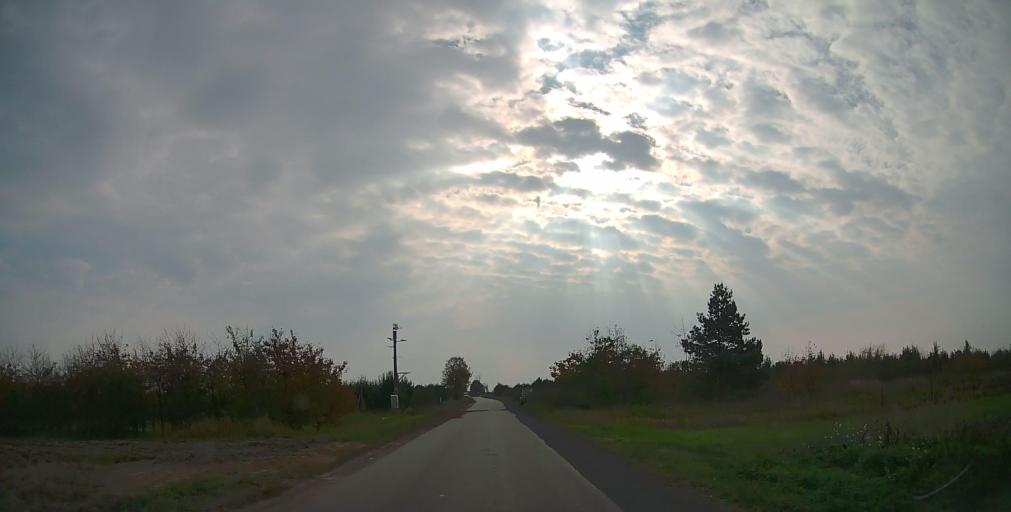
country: PL
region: Masovian Voivodeship
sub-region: Powiat grojecki
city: Mogielnica
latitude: 51.6512
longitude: 20.7261
